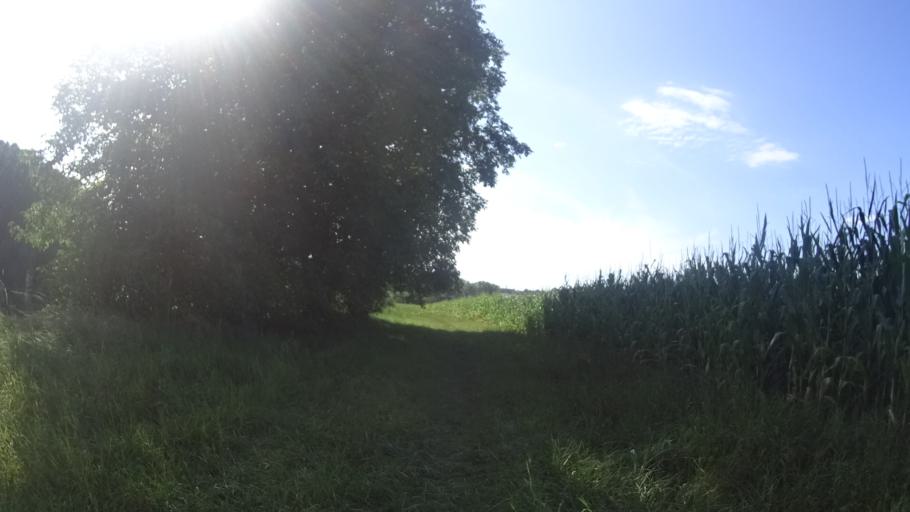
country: FR
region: Franche-Comte
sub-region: Departement du Doubs
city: Thise
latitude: 47.2616
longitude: 6.0757
